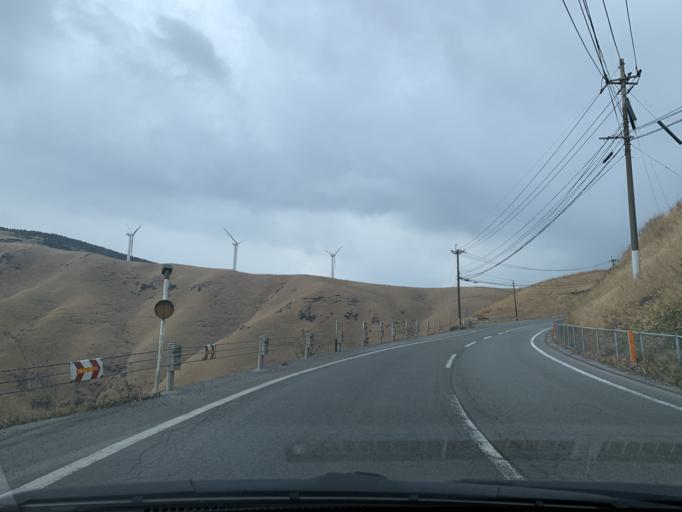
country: JP
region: Kumamoto
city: Ozu
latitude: 32.9122
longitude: 130.9699
